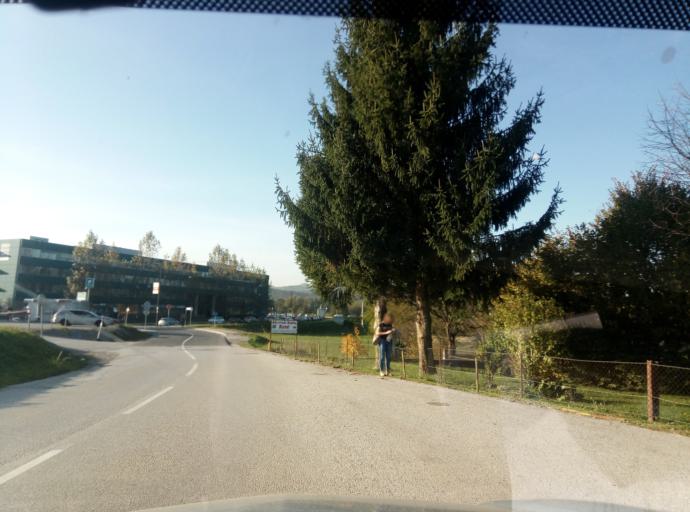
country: SI
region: Ljubljana
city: Ljubljana
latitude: 46.0495
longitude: 14.4622
